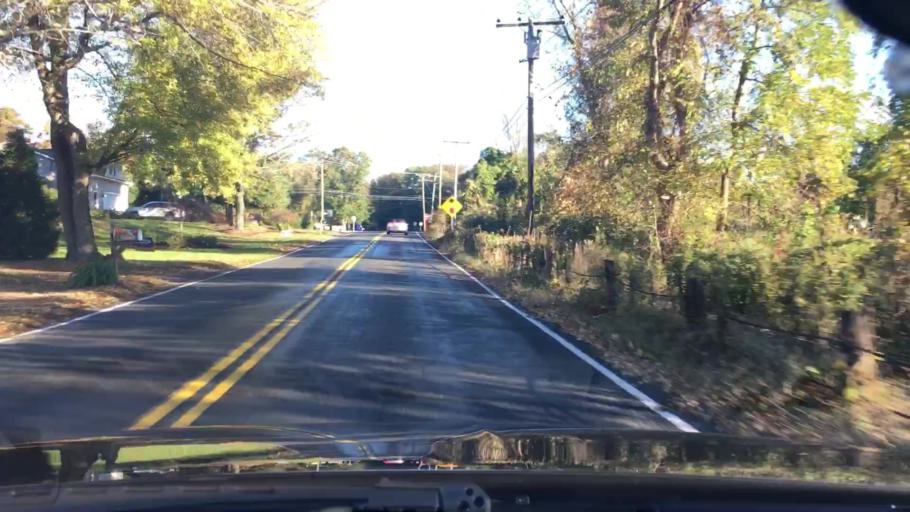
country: US
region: Connecticut
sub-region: Tolland County
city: Somers
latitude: 42.0105
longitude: -72.4817
